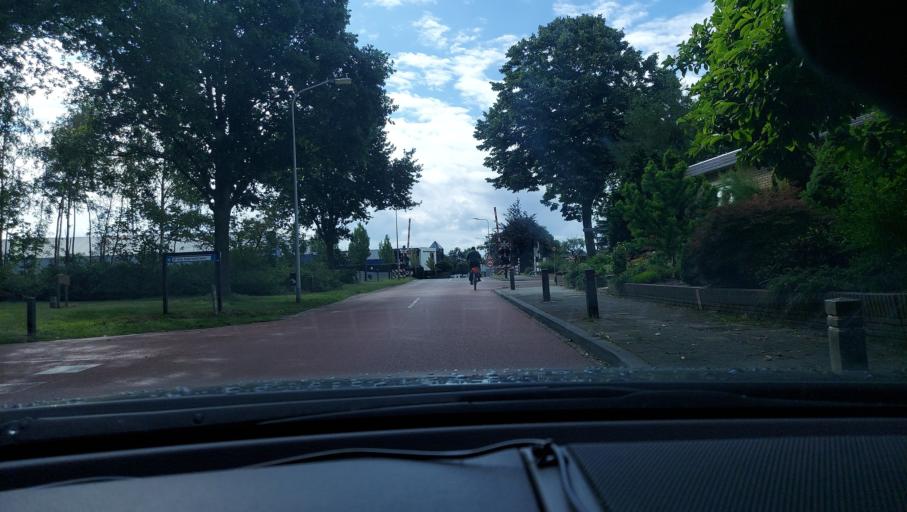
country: NL
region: Limburg
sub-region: Gemeente Beesel
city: Reuver
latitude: 51.2904
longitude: 6.0863
